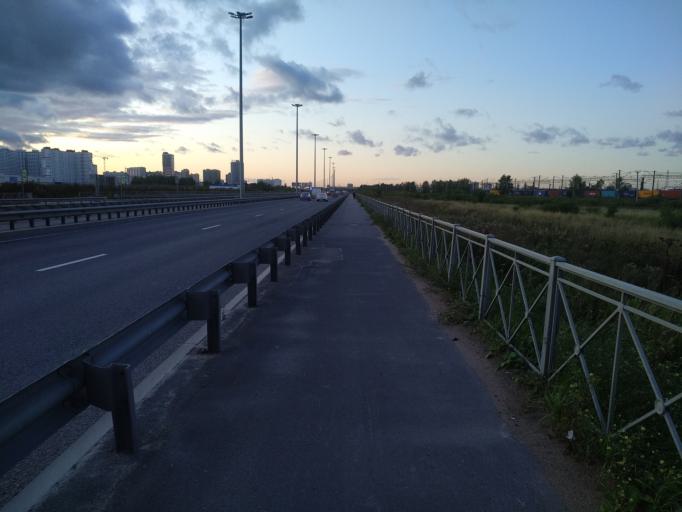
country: RU
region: St.-Petersburg
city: Shushary
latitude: 59.7938
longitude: 30.3925
